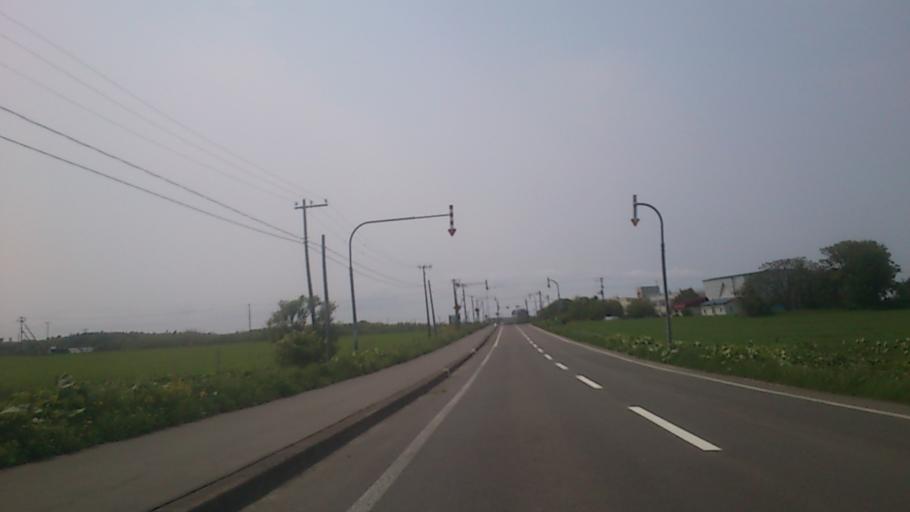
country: JP
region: Hokkaido
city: Nemuro
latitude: 43.2777
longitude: 145.5224
